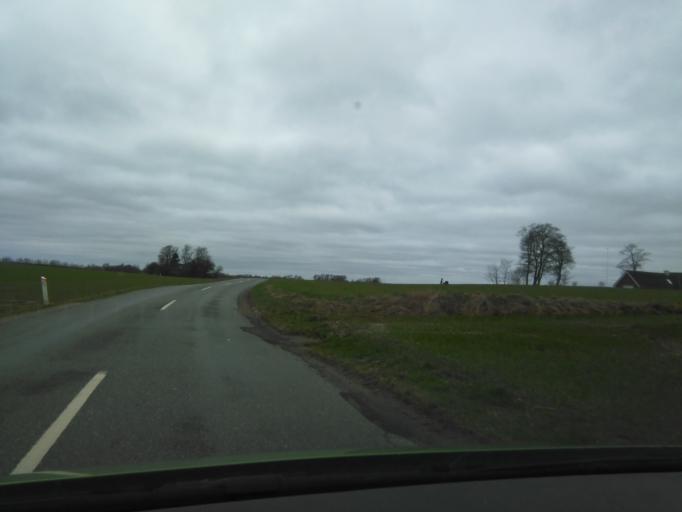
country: DK
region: Central Jutland
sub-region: Arhus Kommune
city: Marslet
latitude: 56.0507
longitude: 10.1326
